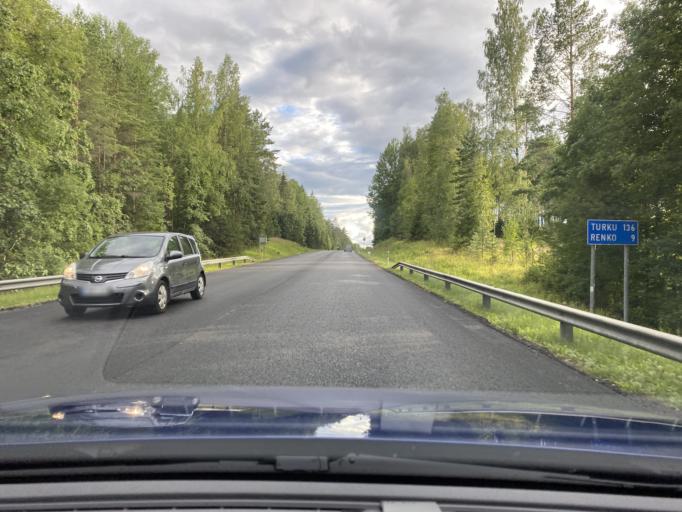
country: FI
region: Haeme
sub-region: Haemeenlinna
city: Haemeenlinna
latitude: 60.9511
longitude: 24.4046
